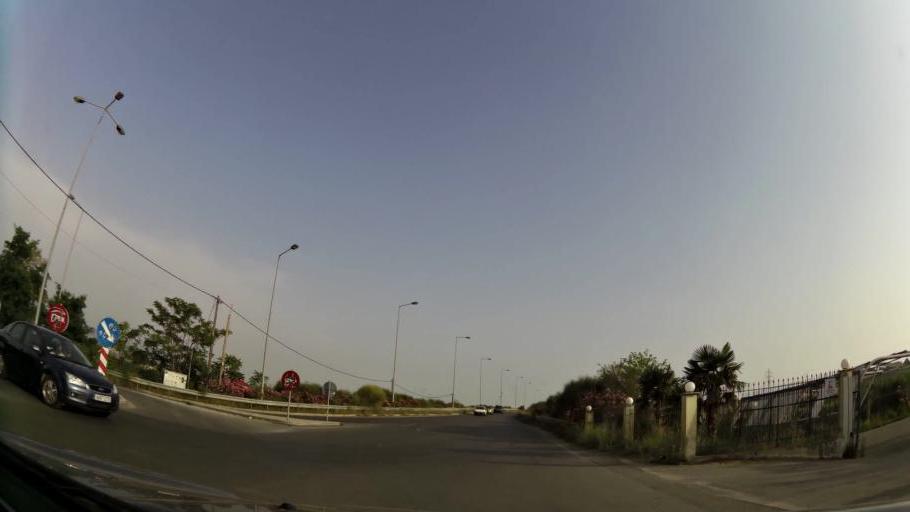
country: GR
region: Central Macedonia
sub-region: Nomos Thessalonikis
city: Evosmos
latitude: 40.6975
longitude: 22.9095
